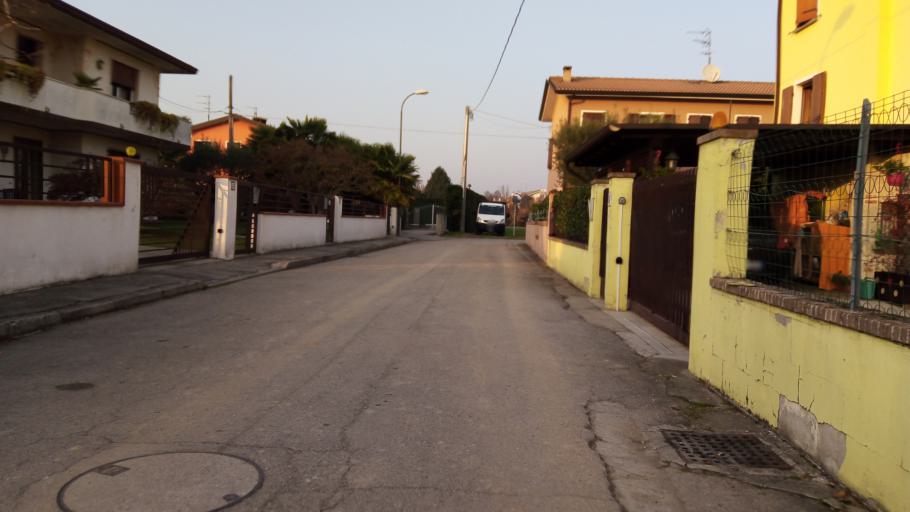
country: IT
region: Veneto
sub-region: Provincia di Padova
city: Abano Terme
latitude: 45.3515
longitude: 11.7695
